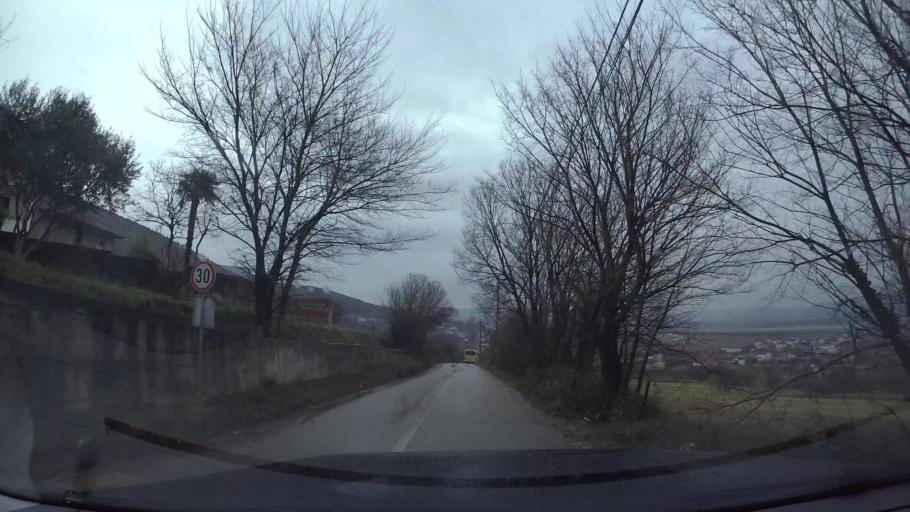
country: BA
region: Federation of Bosnia and Herzegovina
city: Blagaj
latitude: 43.2936
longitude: 17.8577
